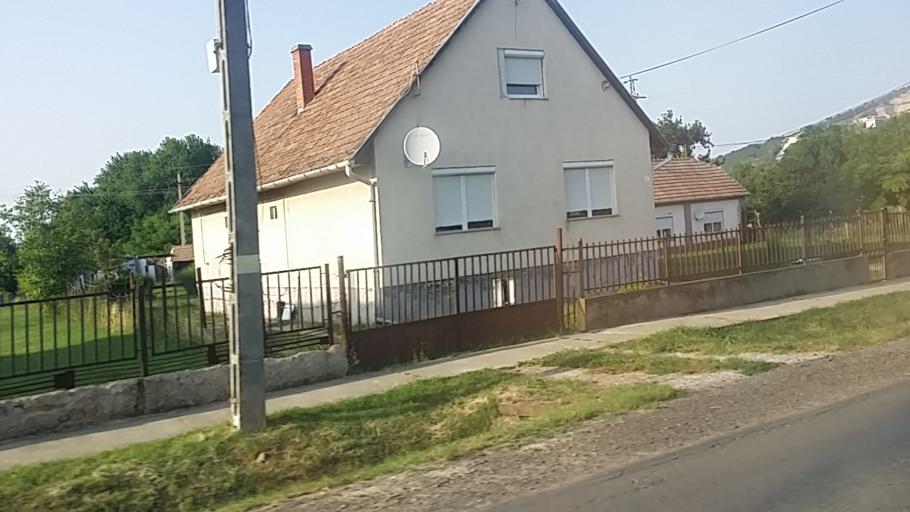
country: HU
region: Baranya
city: Villany
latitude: 45.8482
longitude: 18.3825
